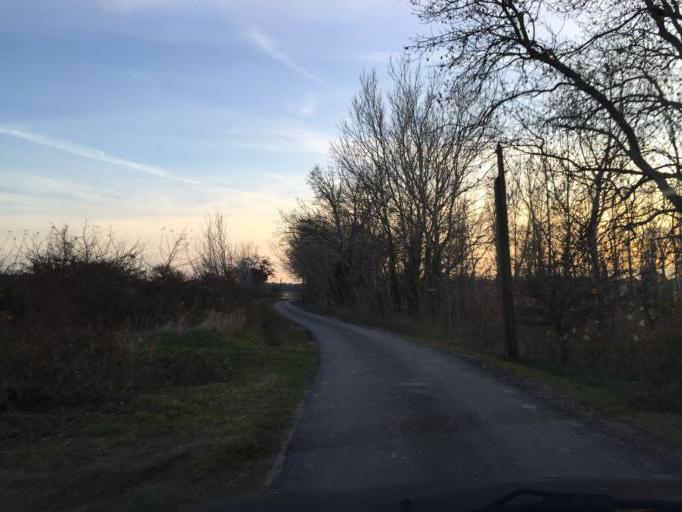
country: FR
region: Provence-Alpes-Cote d'Azur
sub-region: Departement du Vaucluse
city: Jonquieres
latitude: 44.1224
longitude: 4.8566
